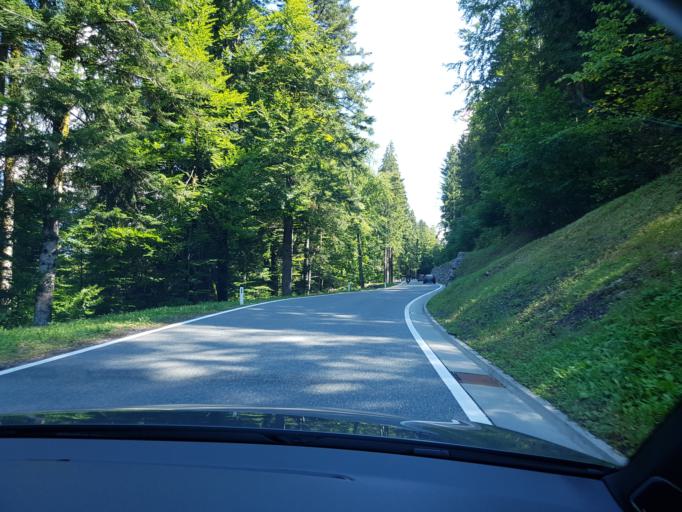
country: AT
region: Vorarlberg
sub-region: Politischer Bezirk Bludenz
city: Raggal
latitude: 47.2094
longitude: 9.8129
